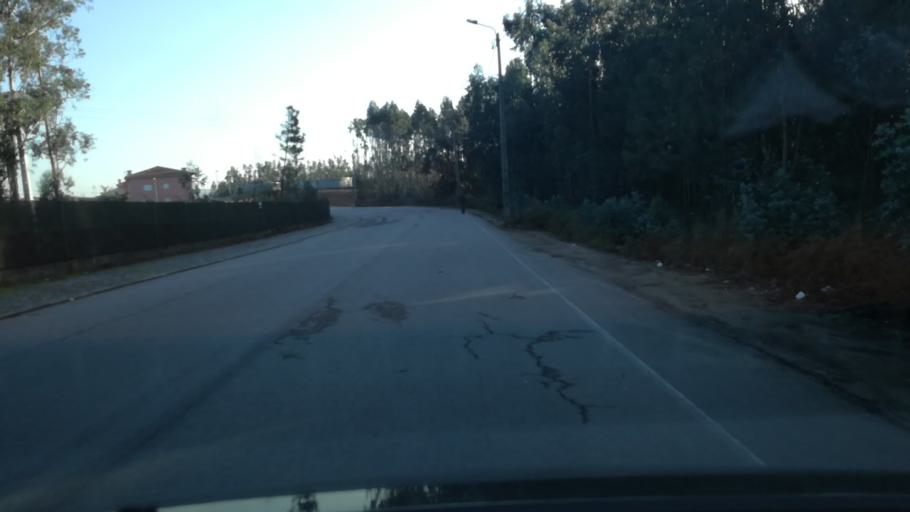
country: PT
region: Braga
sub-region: Vila Nova de Famalicao
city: Ferreiros
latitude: 41.3634
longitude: -8.5328
